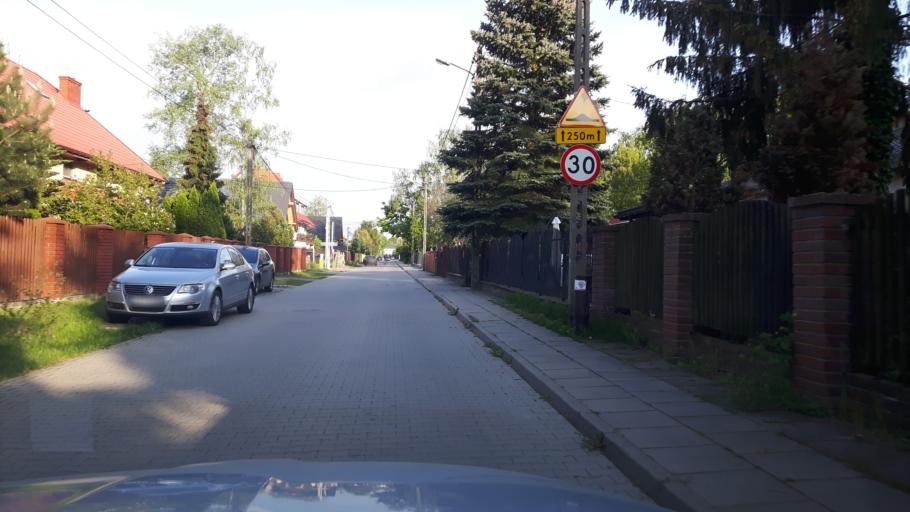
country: PL
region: Masovian Voivodeship
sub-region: Warszawa
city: Rembertow
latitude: 52.2757
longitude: 21.1561
